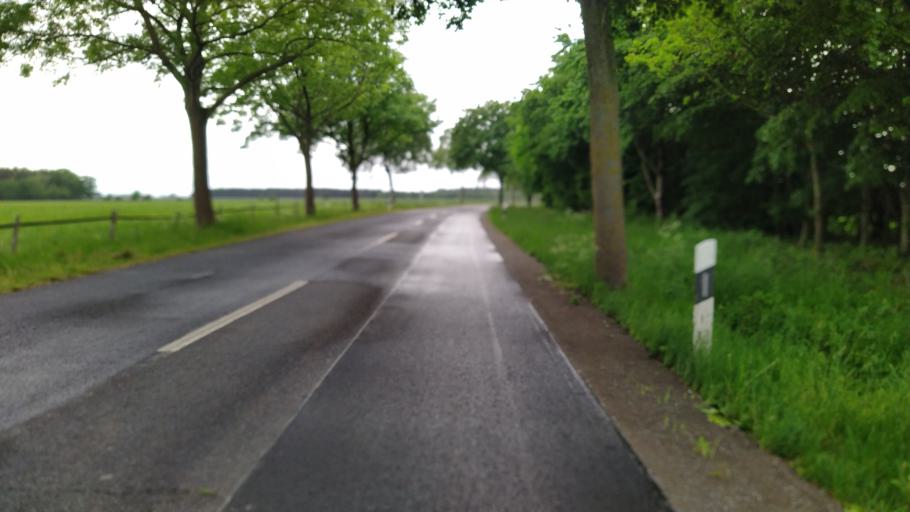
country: DE
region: Lower Saxony
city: Bargstedt
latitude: 53.4548
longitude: 9.4185
